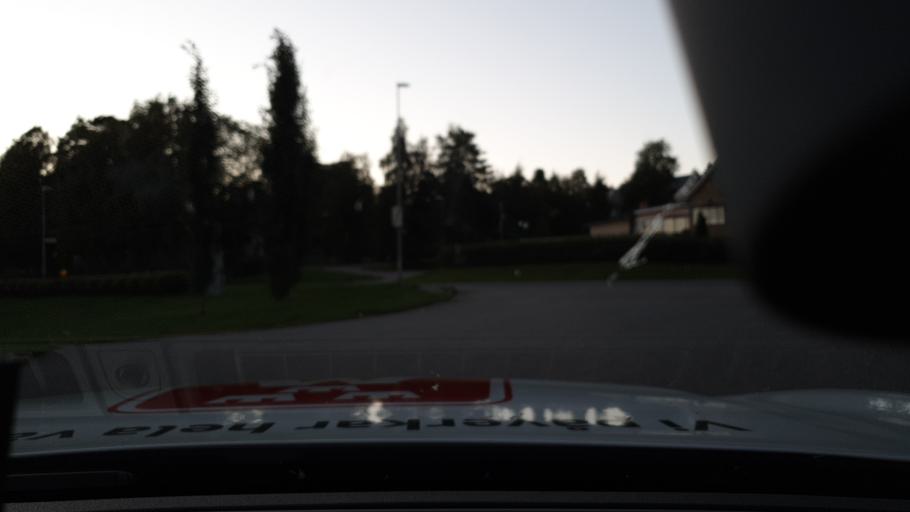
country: SE
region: Norrbotten
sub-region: Lulea Kommun
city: Lulea
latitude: 65.5897
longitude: 22.1856
